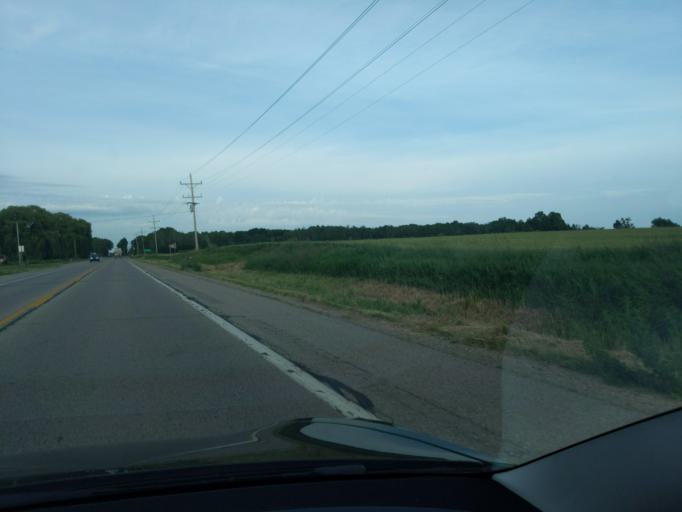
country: US
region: Michigan
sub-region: Montcalm County
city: Edmore
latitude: 43.4079
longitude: -85.1093
